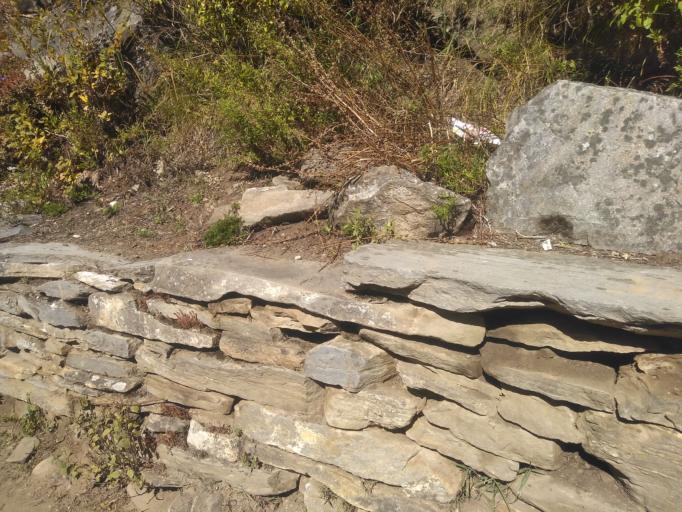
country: NP
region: Western Region
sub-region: Dhawalagiri Zone
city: Jomsom
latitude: 28.9442
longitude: 83.0621
